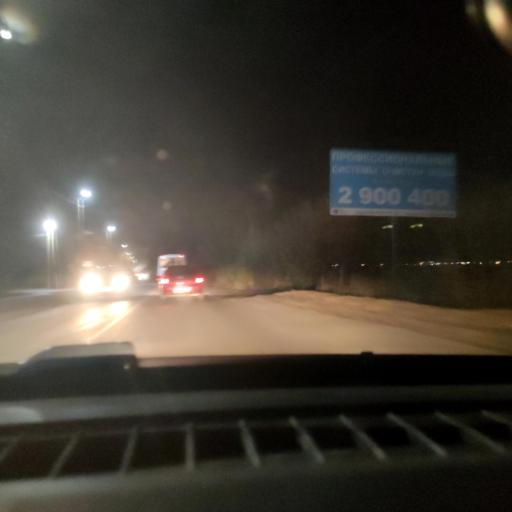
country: RU
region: Voronezj
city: Novaya Usman'
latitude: 51.6541
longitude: 39.3289
